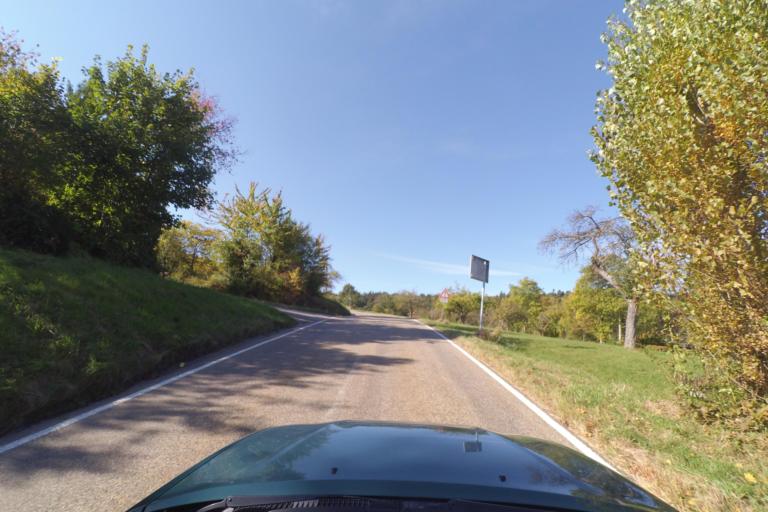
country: DE
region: Baden-Wuerttemberg
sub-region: Karlsruhe Region
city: Simmozheim
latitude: 48.7755
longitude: 8.8105
